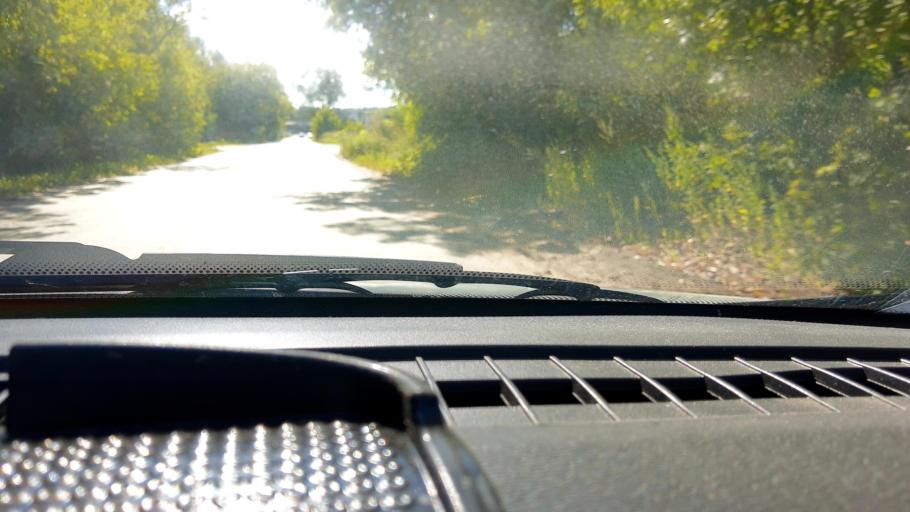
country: RU
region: Nizjnij Novgorod
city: Lukino
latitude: 56.4188
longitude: 43.6460
